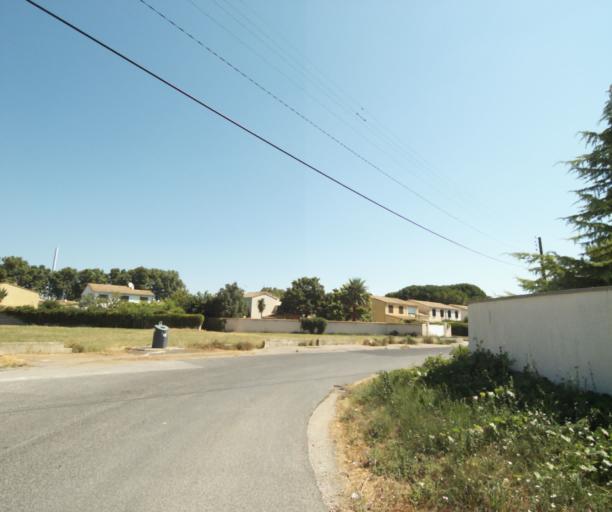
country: FR
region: Languedoc-Roussillon
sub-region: Departement de l'Herault
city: Marsillargues
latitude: 43.6615
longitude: 4.1669
